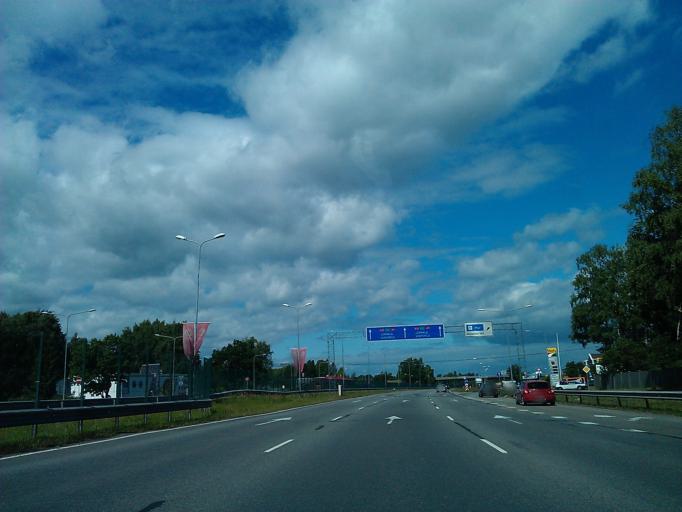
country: LV
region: Marupe
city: Marupe
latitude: 56.9292
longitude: 24.0175
